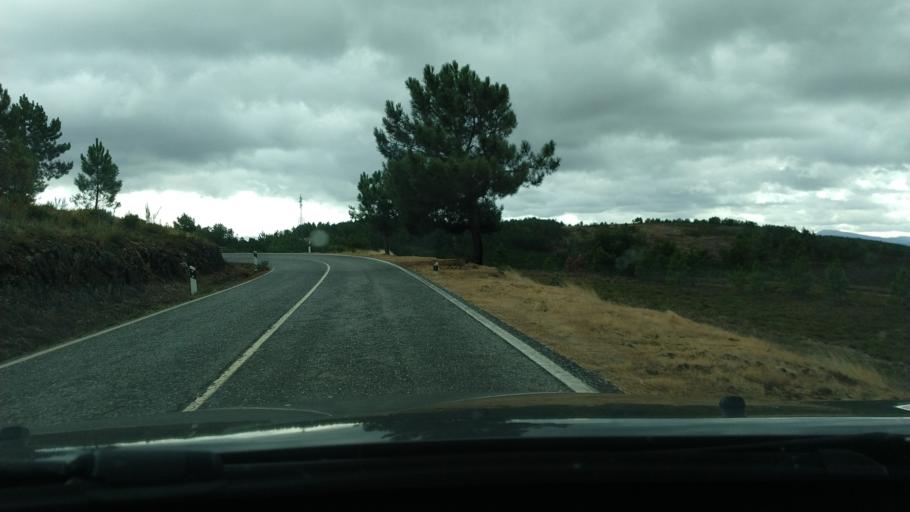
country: PT
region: Castelo Branco
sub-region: Covilha
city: Covilha
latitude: 40.2357
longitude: -7.6754
